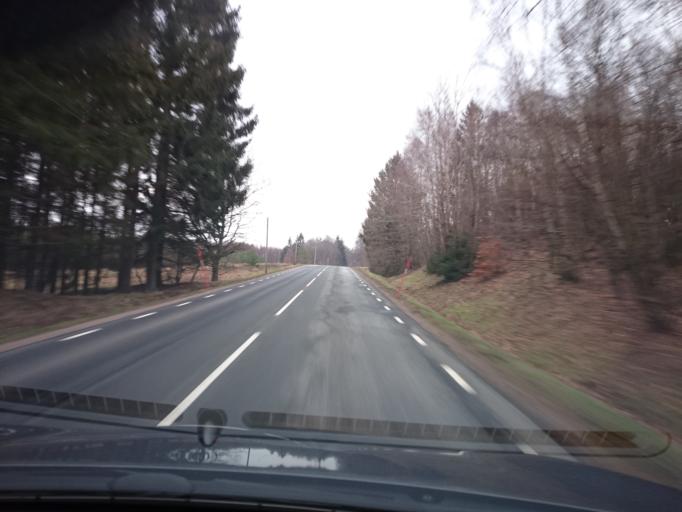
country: SE
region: Skane
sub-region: Hoors Kommun
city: Hoeoer
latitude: 55.9703
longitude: 13.5736
